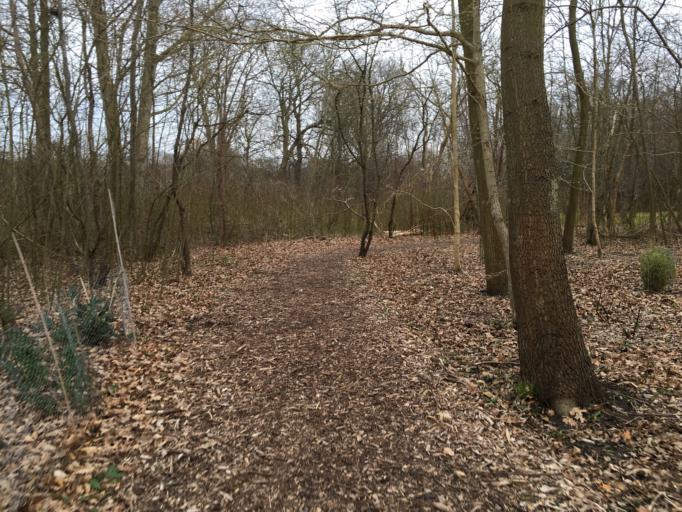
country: SE
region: Skane
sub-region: Lomma Kommun
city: Lomma
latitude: 55.6562
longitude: 13.0751
